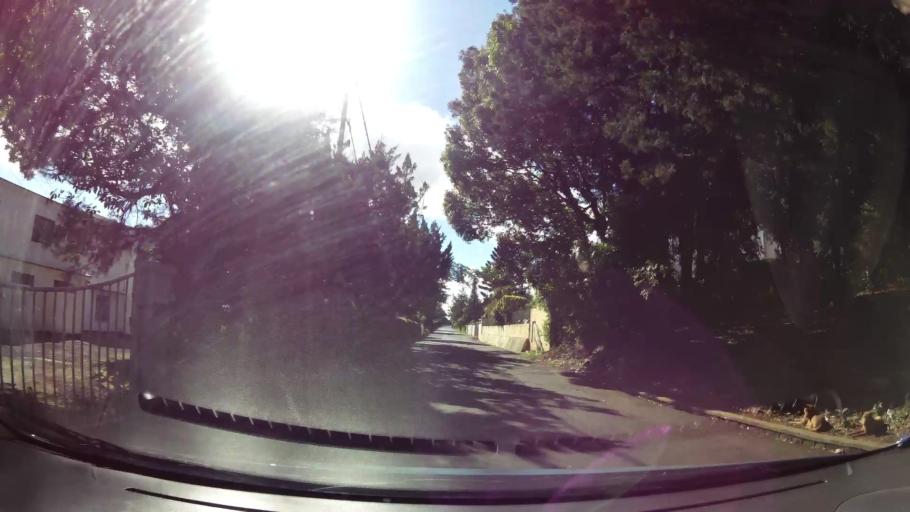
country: MU
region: Plaines Wilhems
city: Curepipe
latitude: -20.3100
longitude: 57.5088
